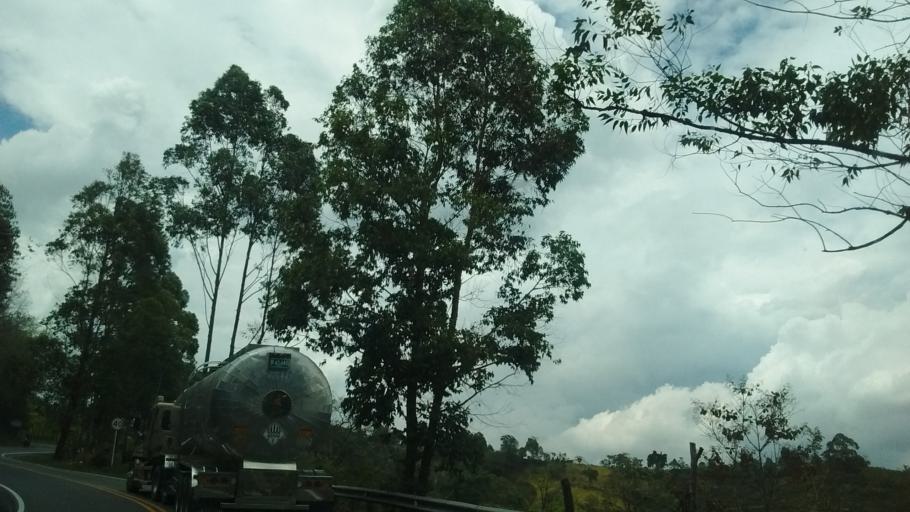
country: CO
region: Cauca
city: Rosas
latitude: 2.3198
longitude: -76.6894
